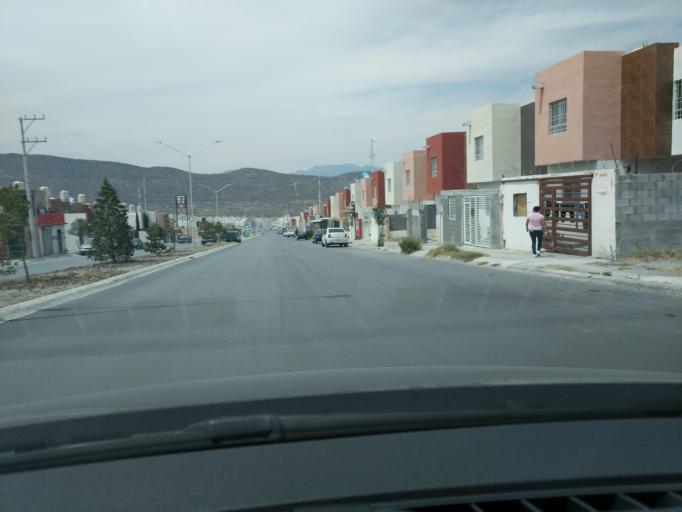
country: MX
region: Coahuila
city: Saltillo
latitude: 25.3627
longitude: -101.0316
